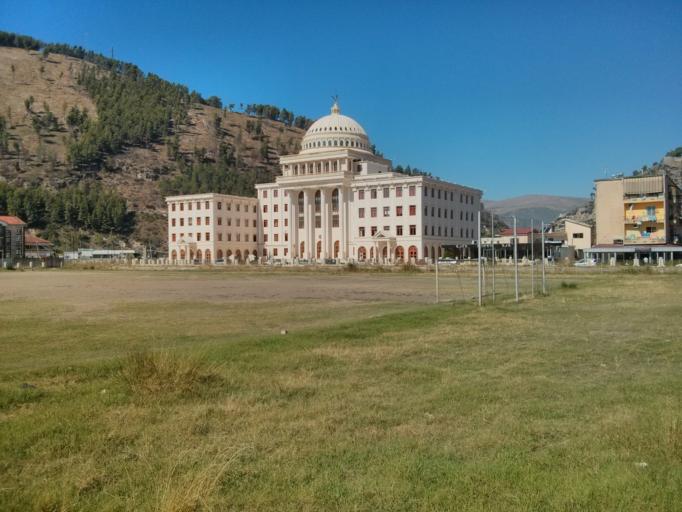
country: AL
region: Berat
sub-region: Rrethi i Beratit
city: Berat
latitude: 40.7014
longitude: 19.9588
